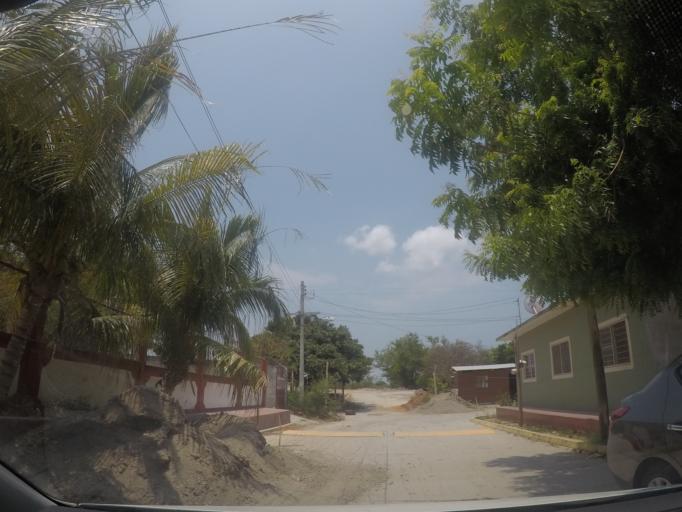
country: MX
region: Oaxaca
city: Asuncion Ixtaltepec
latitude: 16.5061
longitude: -95.0554
